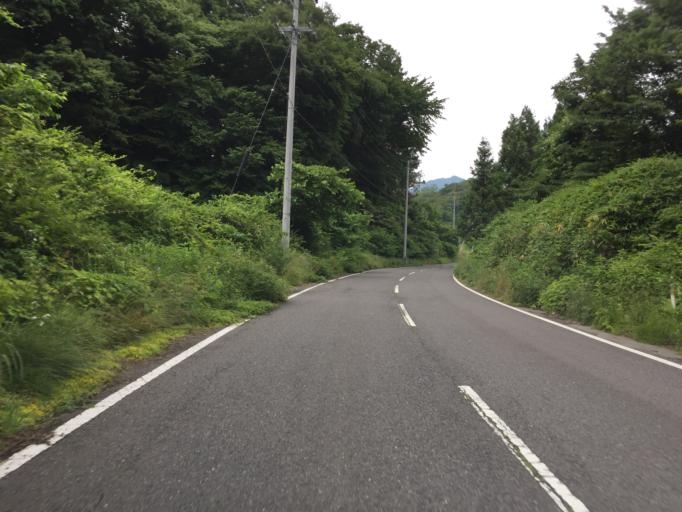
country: JP
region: Fukushima
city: Funehikimachi-funehiki
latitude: 37.4122
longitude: 140.6481
